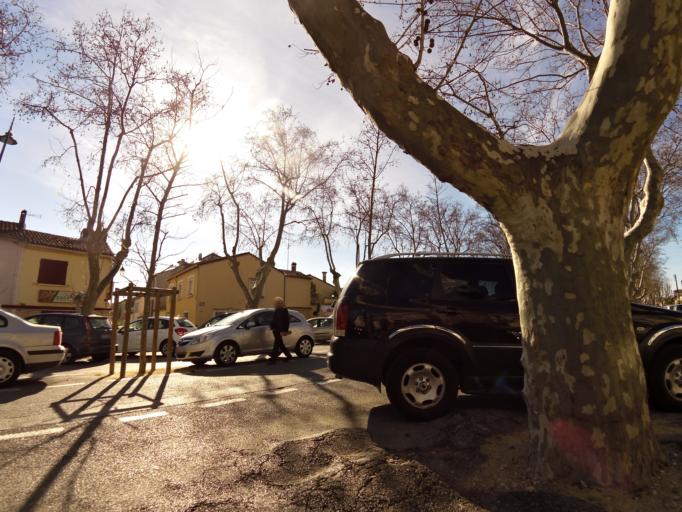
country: FR
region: Languedoc-Roussillon
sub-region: Departement du Gard
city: Aigues-Mortes
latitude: 43.5686
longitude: 4.1950
